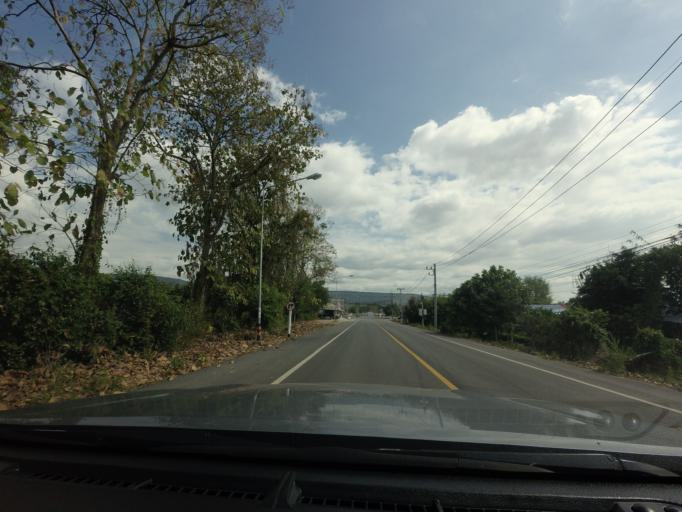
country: TH
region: Phitsanulok
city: Wang Thong
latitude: 16.7407
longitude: 100.4307
